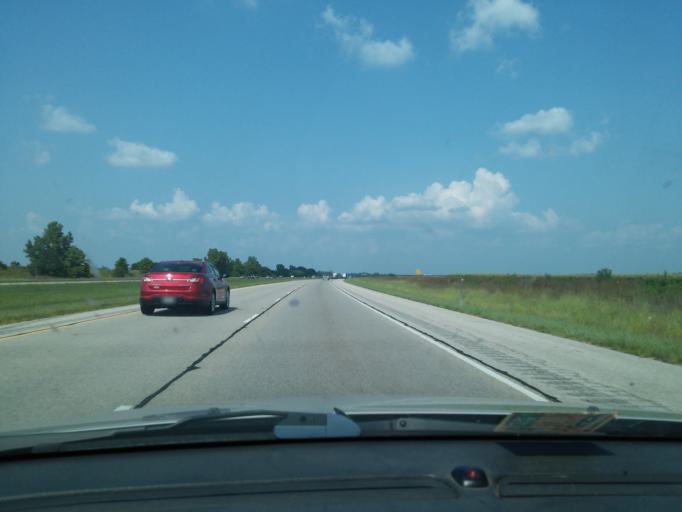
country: US
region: Illinois
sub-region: McLean County
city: Twin Grove
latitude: 40.3796
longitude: -89.0923
